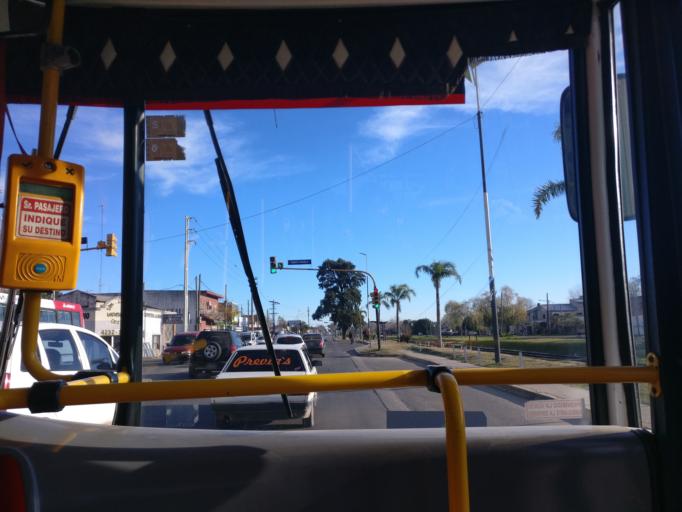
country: AR
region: Buenos Aires
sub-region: Partido de Ezeiza
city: Ezeiza
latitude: -34.8625
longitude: -58.5332
